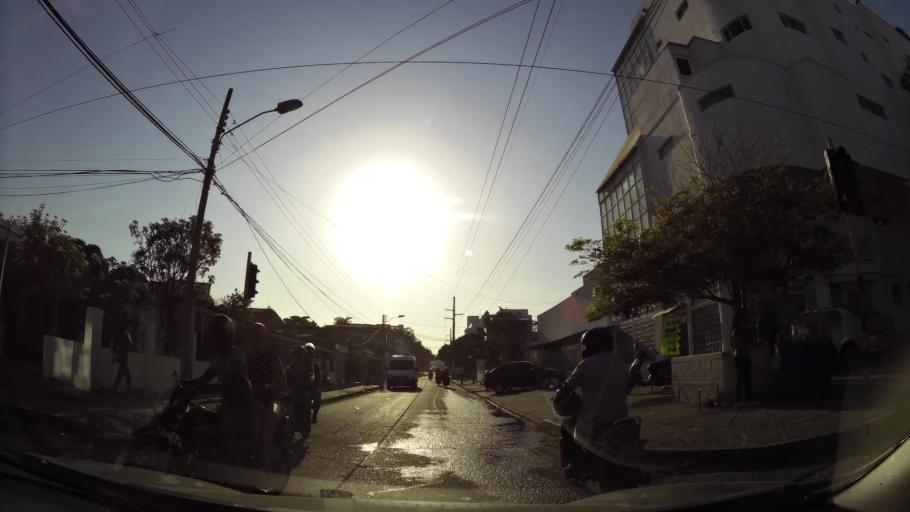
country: CO
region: Bolivar
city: Cartagena
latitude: 10.4067
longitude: -75.5148
